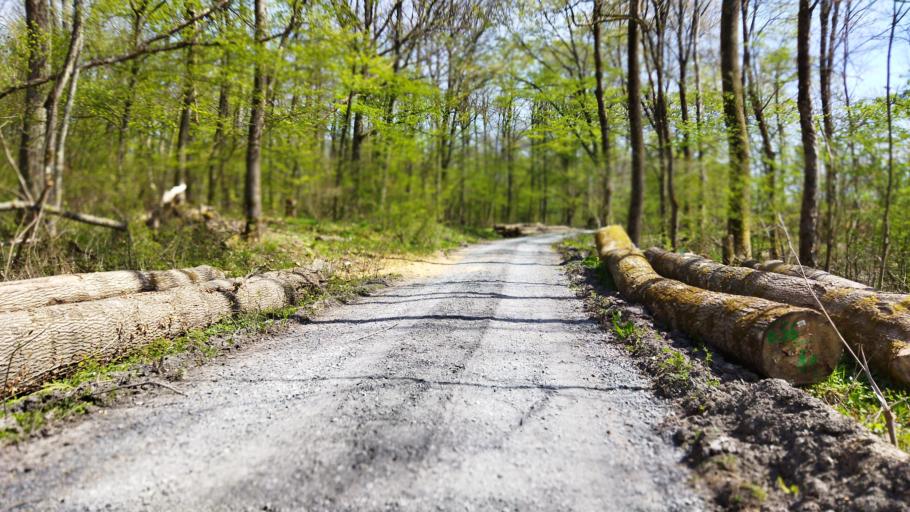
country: DE
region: Baden-Wuerttemberg
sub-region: Regierungsbezirk Stuttgart
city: Pfaffenhofen
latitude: 49.0810
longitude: 8.9703
